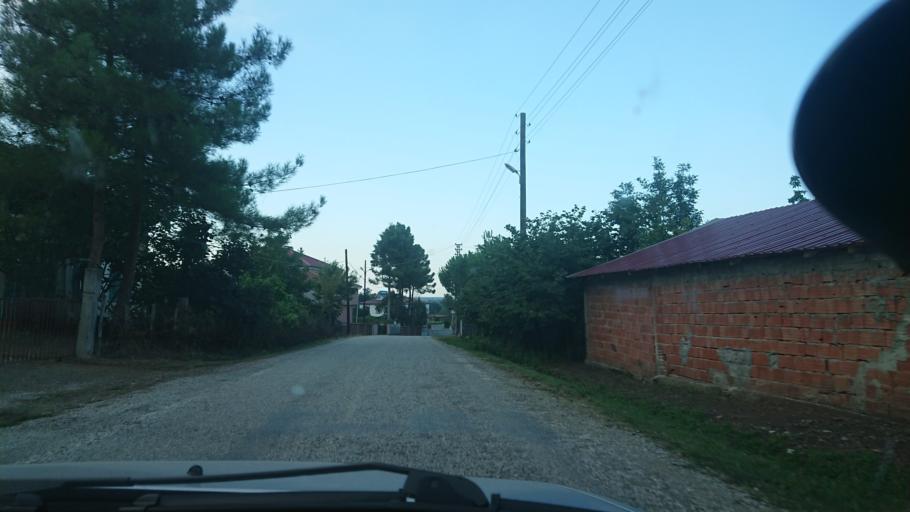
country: TR
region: Samsun
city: Dikbiyik
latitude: 41.1752
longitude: 36.5423
